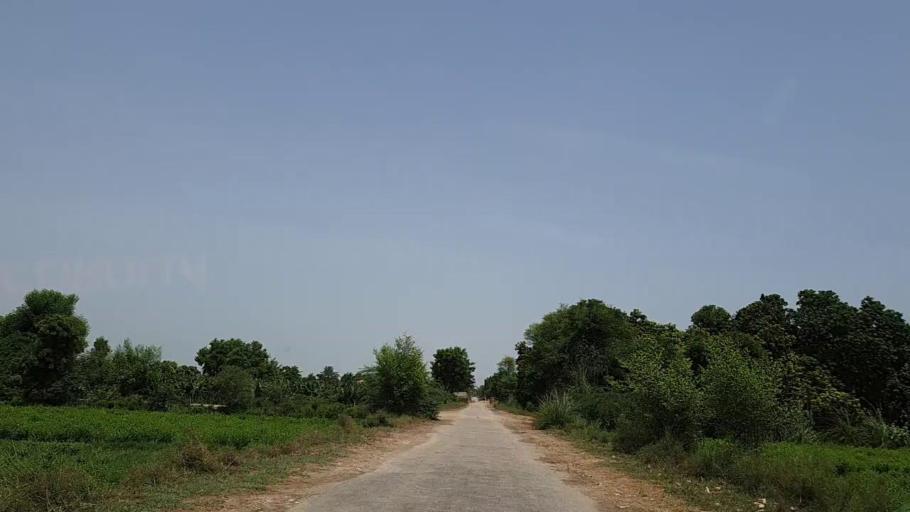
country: PK
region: Sindh
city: Tharu Shah
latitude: 26.9482
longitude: 68.0255
